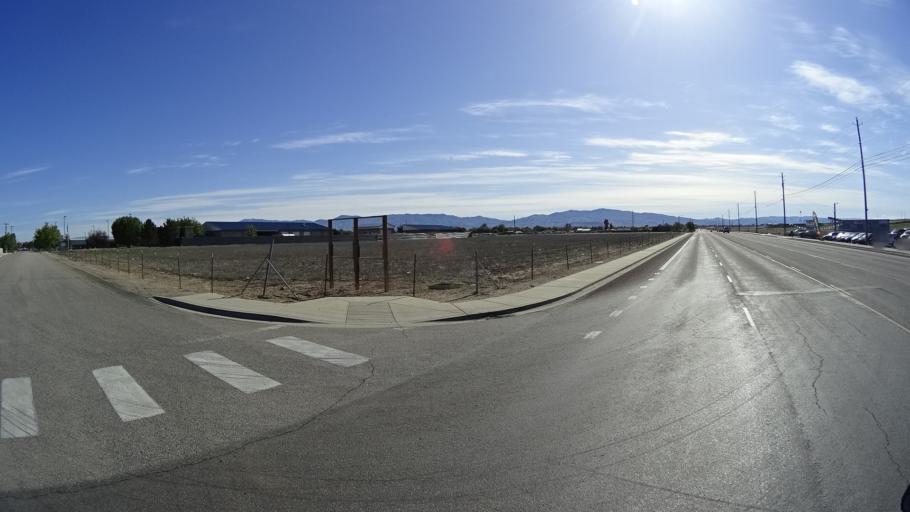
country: US
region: Idaho
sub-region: Ada County
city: Garden City
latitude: 43.5755
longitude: -116.2611
